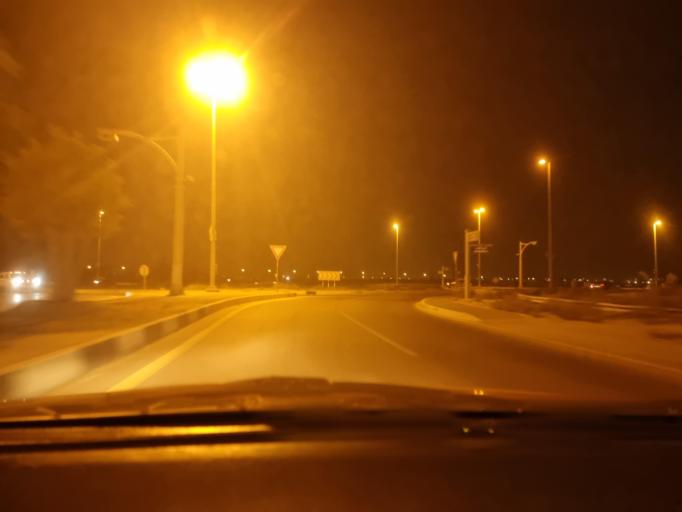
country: AE
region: Abu Dhabi
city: Abu Dhabi
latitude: 24.3861
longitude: 54.6804
